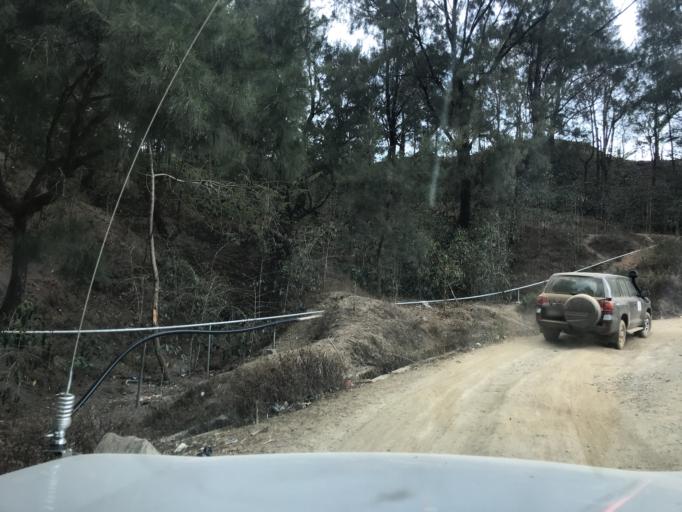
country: TL
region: Ermera
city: Gleno
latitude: -8.8303
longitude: 125.4531
